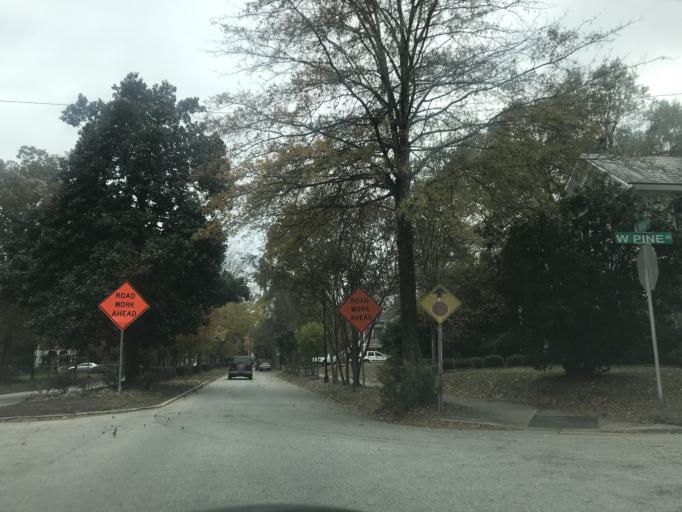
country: US
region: North Carolina
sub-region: Wake County
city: Wake Forest
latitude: 35.9830
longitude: -78.5095
